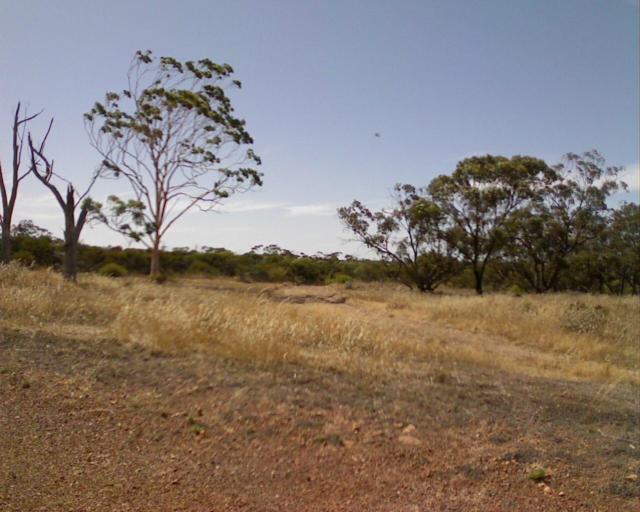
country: AU
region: Western Australia
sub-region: Moora
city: Moora
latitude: -30.1503
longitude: 116.0847
